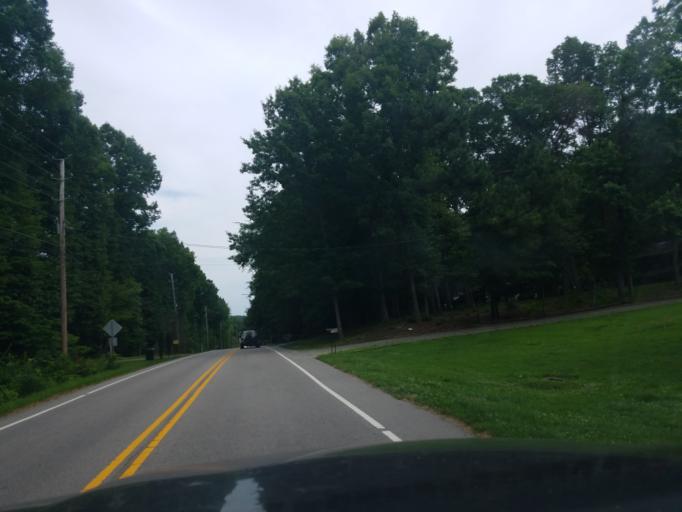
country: US
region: North Carolina
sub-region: Durham County
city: Durham
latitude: 36.1268
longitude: -78.9450
